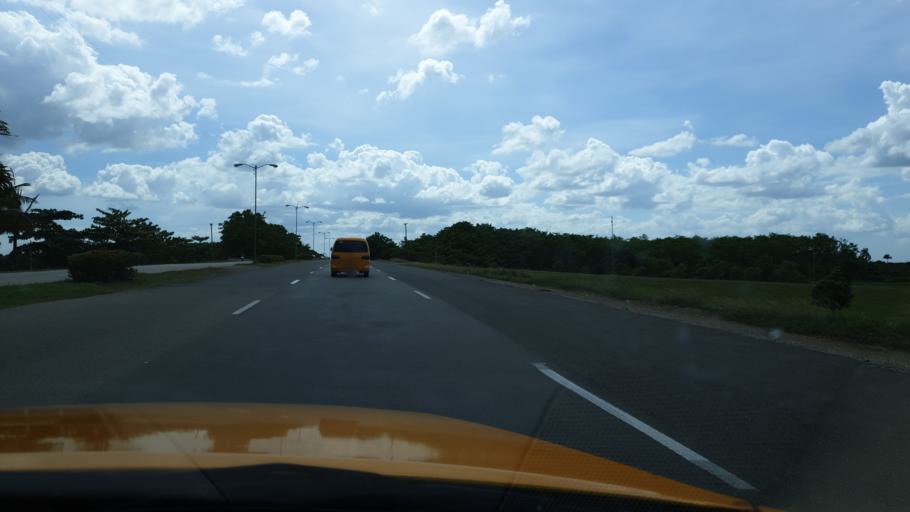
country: CU
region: Cienfuegos
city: Cruces
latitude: 22.4531
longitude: -80.2914
